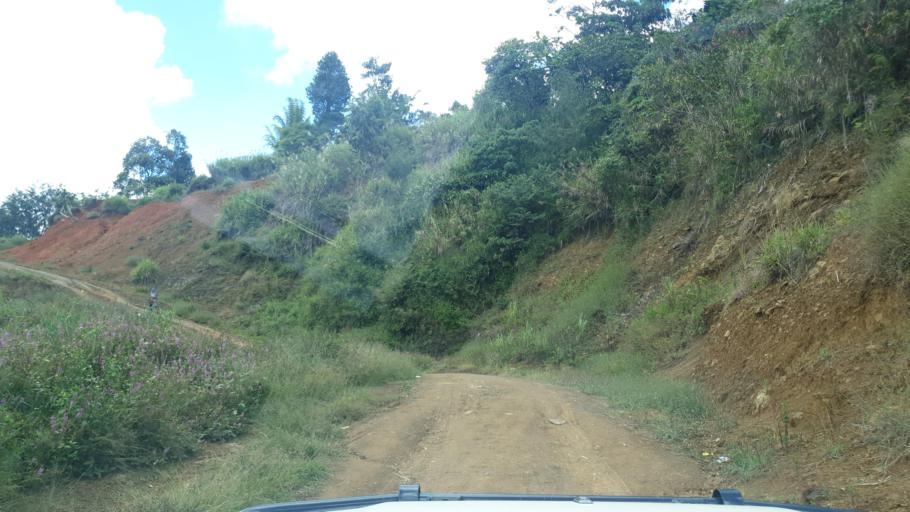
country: PG
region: Eastern Highlands
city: Goroka
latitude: -6.2755
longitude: 145.1886
